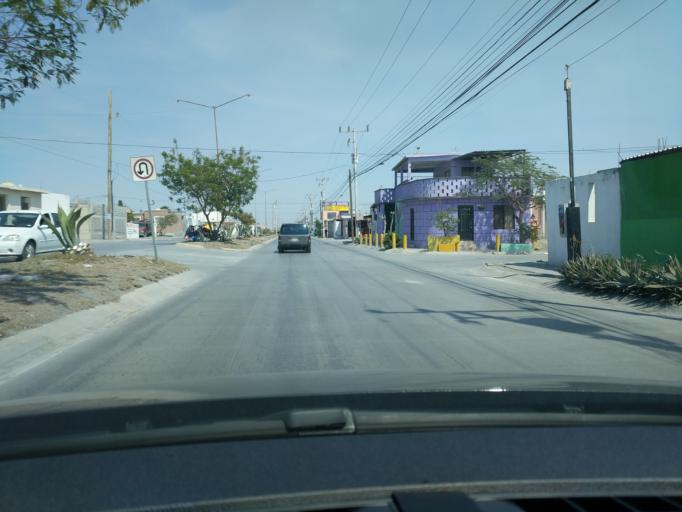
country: MX
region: Nuevo Leon
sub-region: Garcia
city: Valle de Lincoln
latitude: 25.7911
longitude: -100.4862
